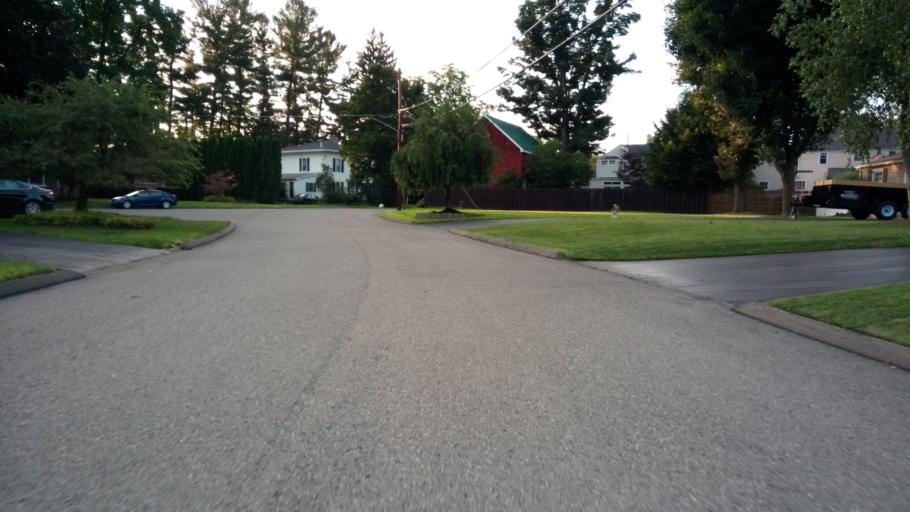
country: US
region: New York
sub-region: Chemung County
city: West Elmira
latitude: 42.0764
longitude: -76.8511
